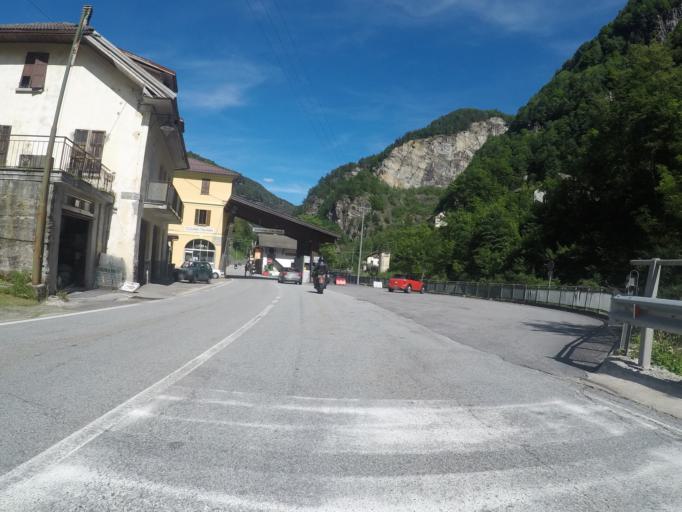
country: IT
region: Piedmont
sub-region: Provincia Verbano-Cusio-Ossola
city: Trasquera
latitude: 46.2043
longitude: 8.1891
